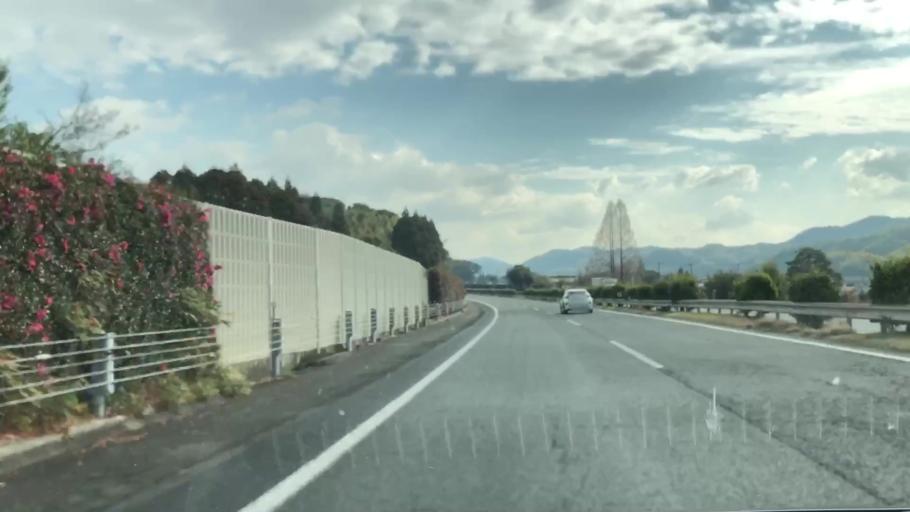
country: JP
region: Fukuoka
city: Setakamachi-takayanagi
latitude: 33.1236
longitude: 130.5193
